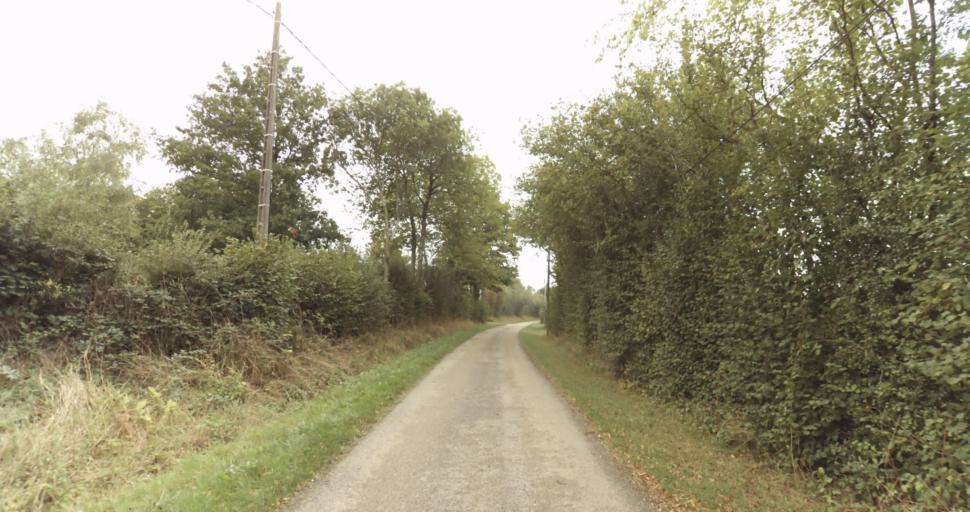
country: FR
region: Lower Normandy
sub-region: Departement de l'Orne
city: Sainte-Gauburge-Sainte-Colombe
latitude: 48.7632
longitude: 0.3781
